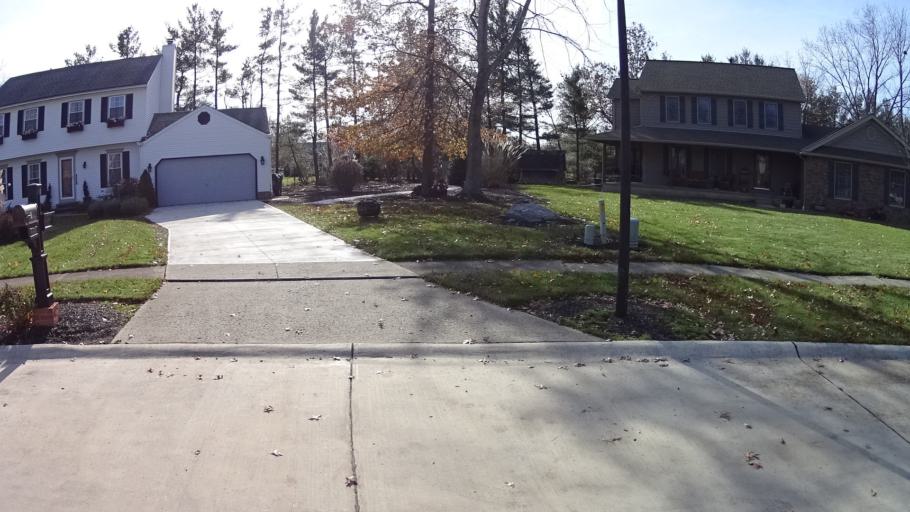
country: US
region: Ohio
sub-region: Lorain County
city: Avon Lake
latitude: 41.4953
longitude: -81.9899
